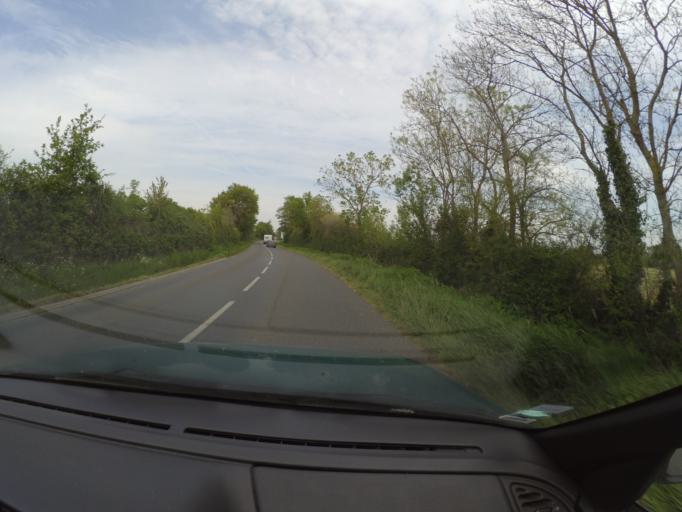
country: FR
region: Pays de la Loire
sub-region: Departement de la Loire-Atlantique
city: Clisson
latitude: 47.0756
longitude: -1.2958
